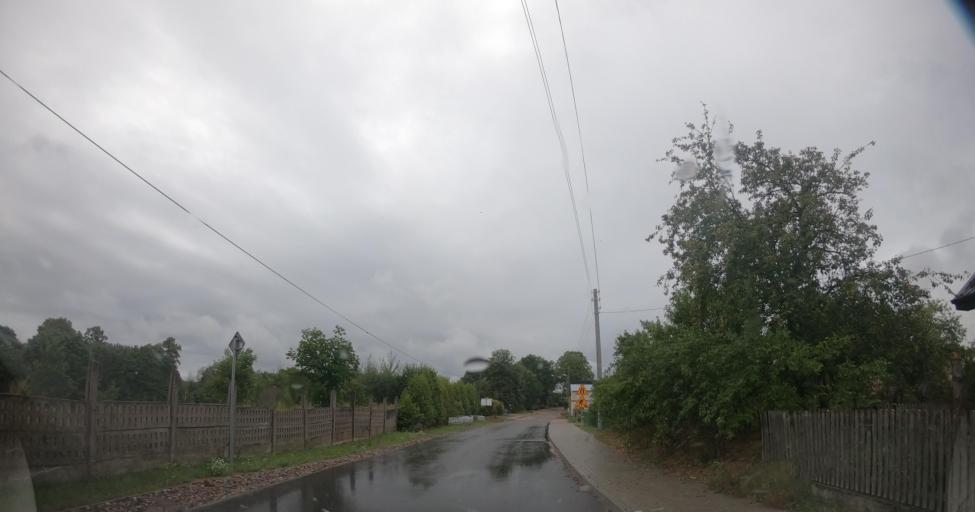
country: PL
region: West Pomeranian Voivodeship
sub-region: Powiat lobeski
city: Wegorzyno
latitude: 53.5376
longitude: 15.5326
